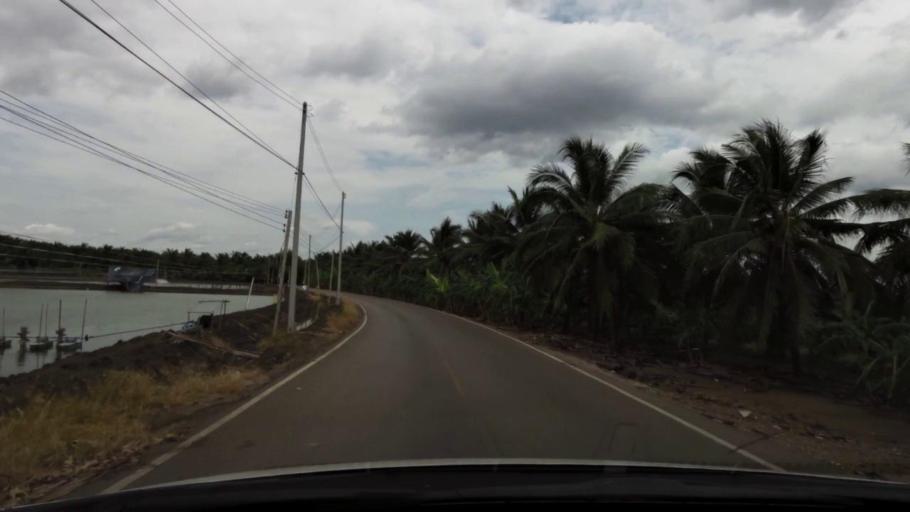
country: TH
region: Samut Sakhon
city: Ban Phaeo
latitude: 13.5758
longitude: 100.0299
